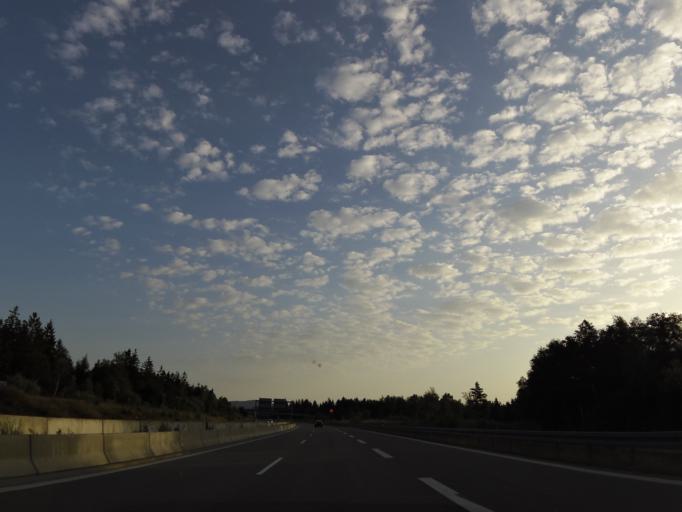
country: AT
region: Tyrol
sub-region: Politischer Bezirk Reutte
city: Vils
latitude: 47.5769
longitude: 10.6621
